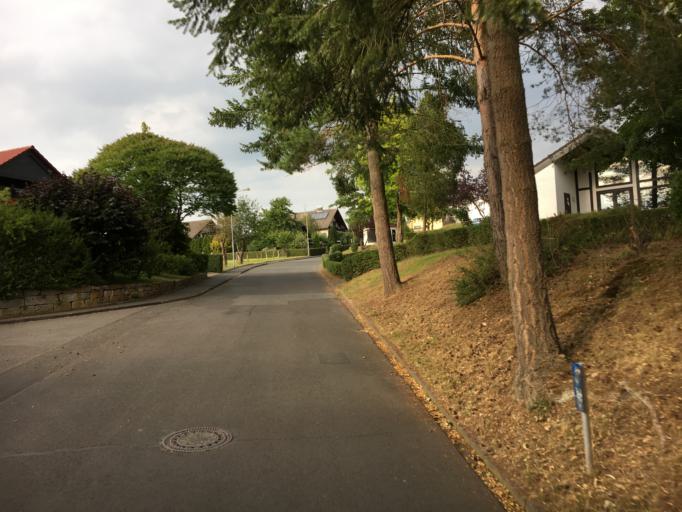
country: DE
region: Hesse
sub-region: Regierungsbezirk Kassel
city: Schrecksbach
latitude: 50.8563
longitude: 9.2936
